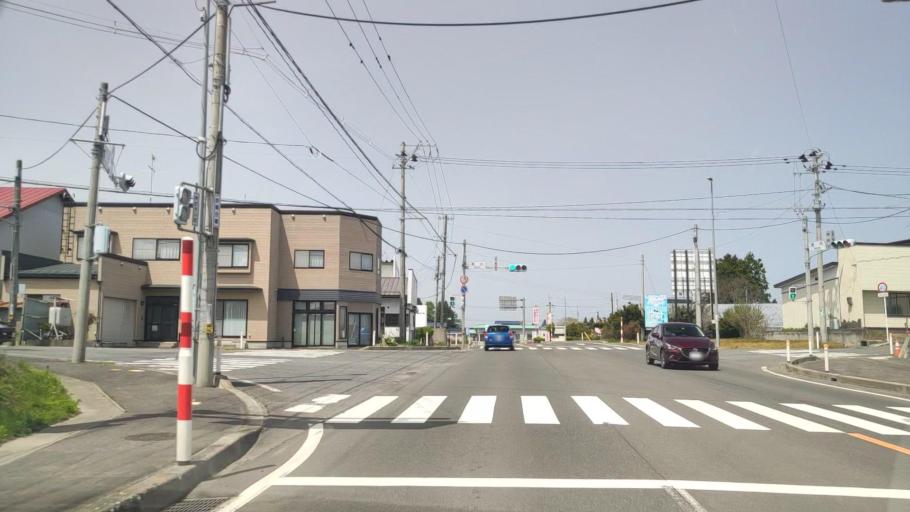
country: JP
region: Aomori
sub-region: Misawa Shi
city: Inuotose
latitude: 40.6582
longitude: 141.1921
